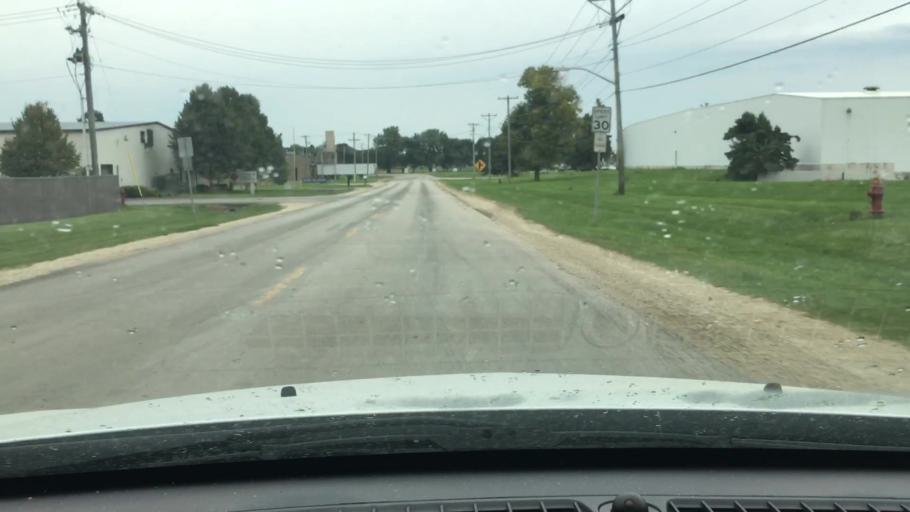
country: US
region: Illinois
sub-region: Ogle County
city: Rochelle
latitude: 41.9058
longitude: -89.0539
